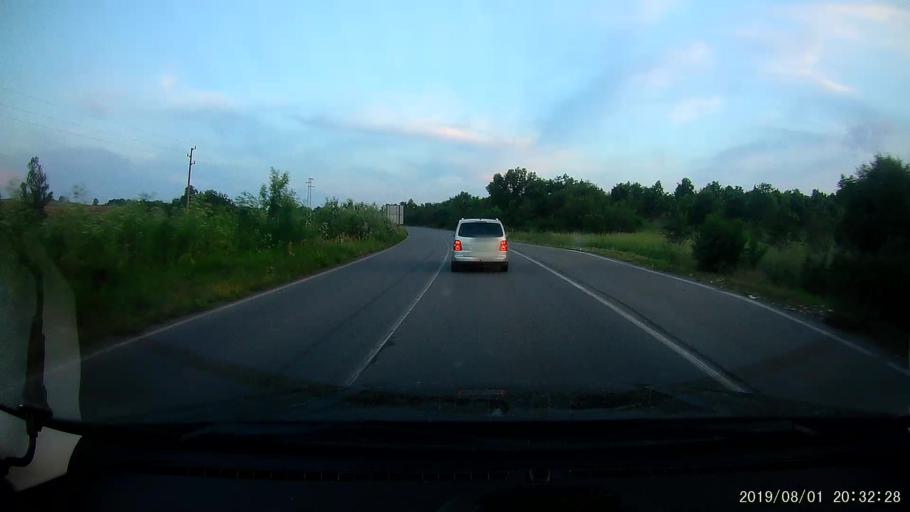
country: BG
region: Yambol
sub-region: Obshtina Elkhovo
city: Elkhovo
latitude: 42.1216
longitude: 26.5298
